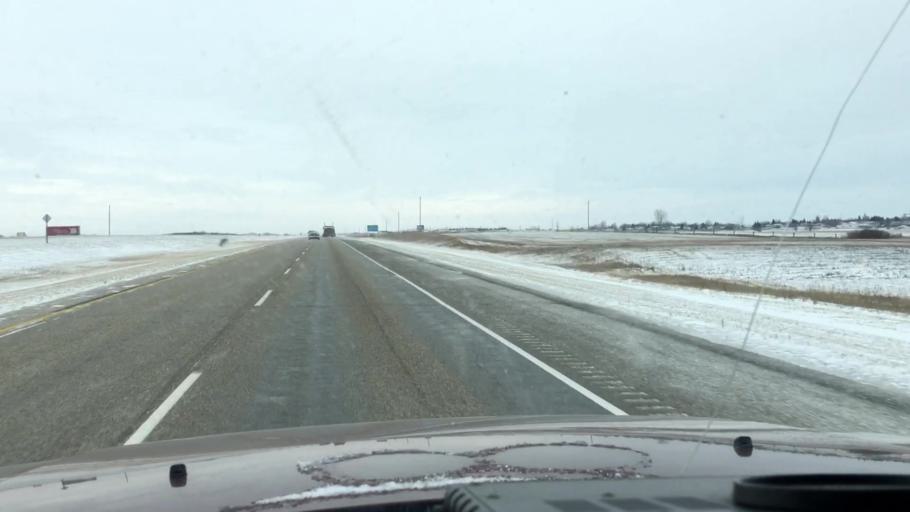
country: CA
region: Saskatchewan
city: Saskatoon
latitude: 51.6437
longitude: -106.4365
